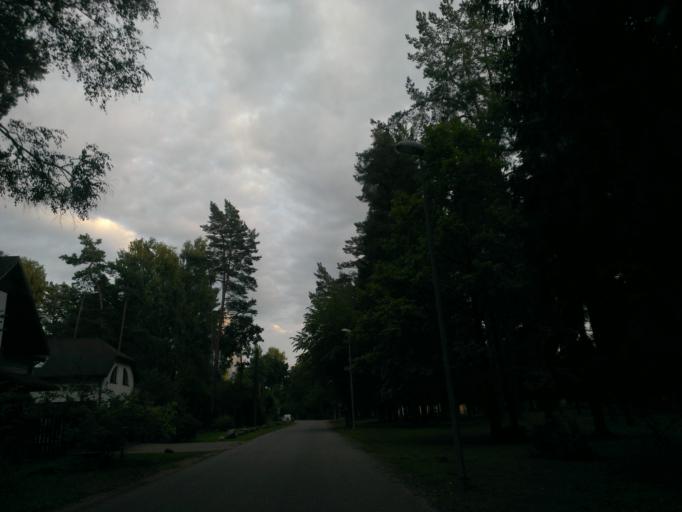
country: LV
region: Ogre
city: Ogre
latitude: 56.8248
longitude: 24.5836
